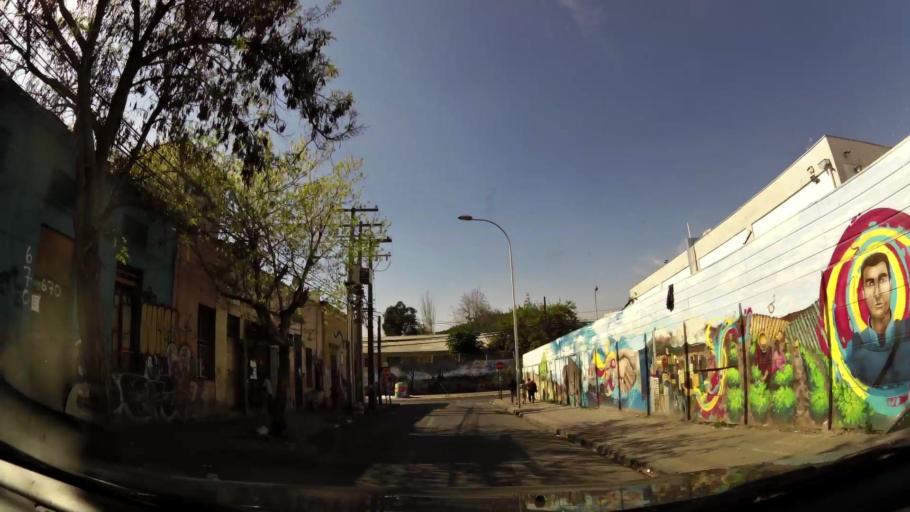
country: CL
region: Santiago Metropolitan
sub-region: Provincia de Santiago
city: Santiago
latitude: -33.4244
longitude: -70.6490
